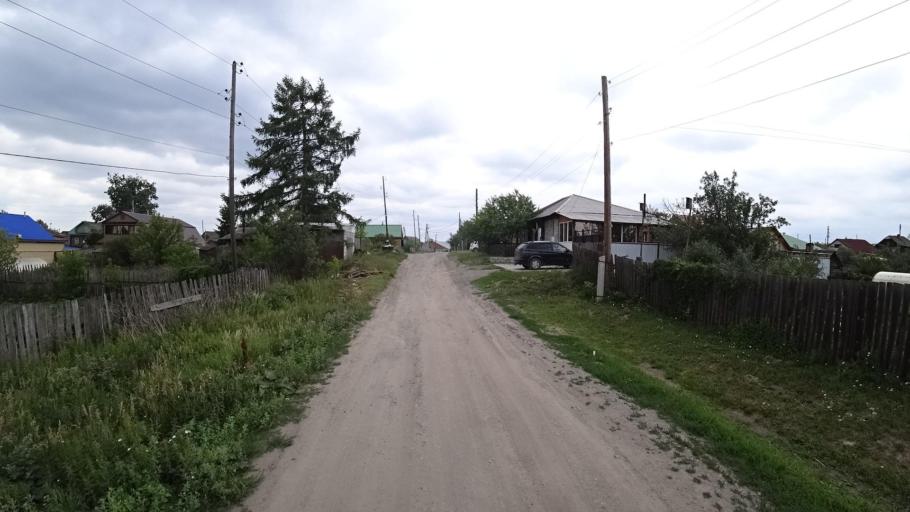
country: RU
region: Sverdlovsk
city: Kamyshlov
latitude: 56.8504
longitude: 62.6798
